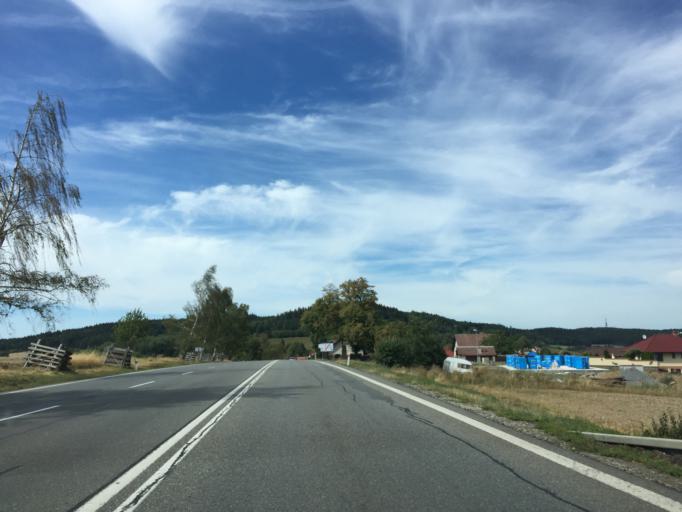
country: CZ
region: Central Bohemia
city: Votice
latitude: 49.5660
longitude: 14.6609
